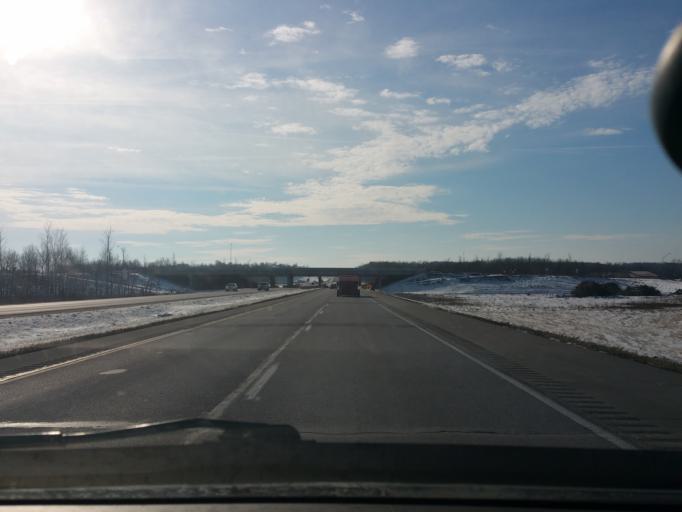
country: US
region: Iowa
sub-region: Warren County
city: Norwalk
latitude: 41.3657
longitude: -93.7805
